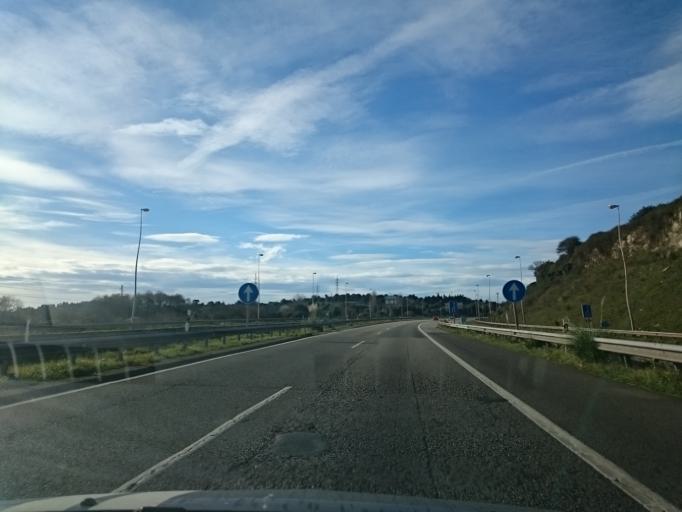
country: ES
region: Asturias
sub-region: Province of Asturias
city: Natahoyo
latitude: 43.5188
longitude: -5.7043
